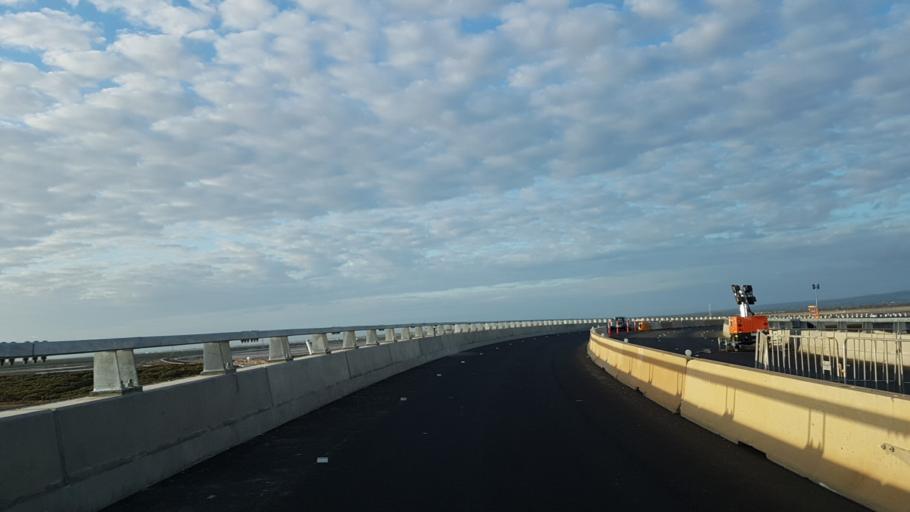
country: AU
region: South Australia
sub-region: Port Adelaide Enfield
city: Blair Athol
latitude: -34.8299
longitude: 138.5620
